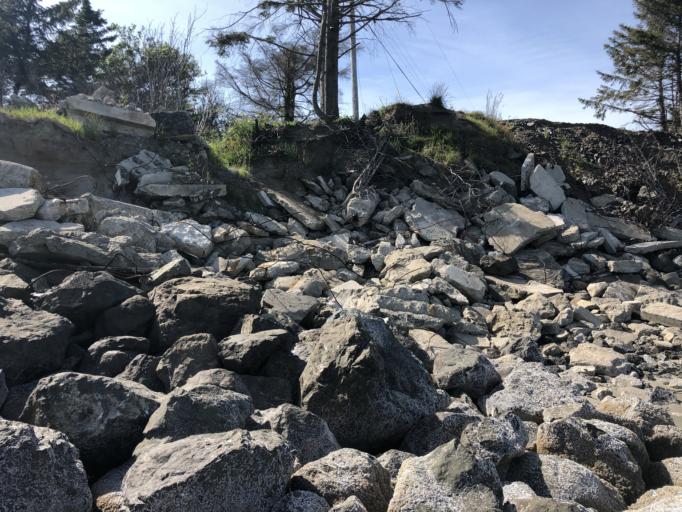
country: US
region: Washington
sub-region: Grays Harbor County
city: Westport
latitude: 46.7365
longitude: -124.0755
